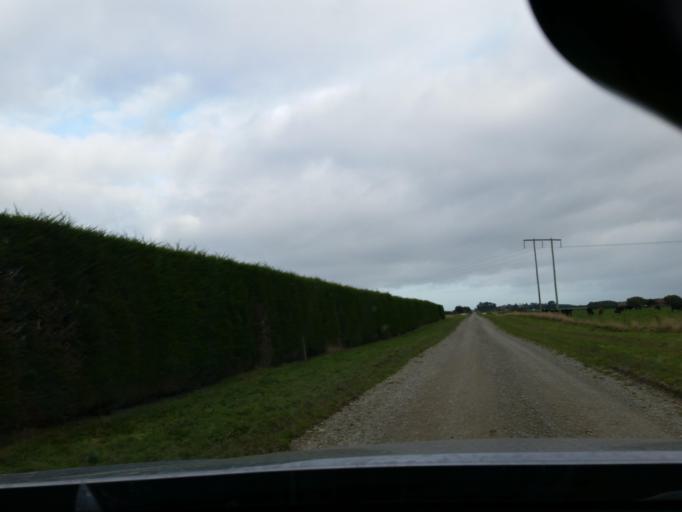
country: NZ
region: Southland
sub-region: Southland District
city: Winton
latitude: -46.2548
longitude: 168.3673
